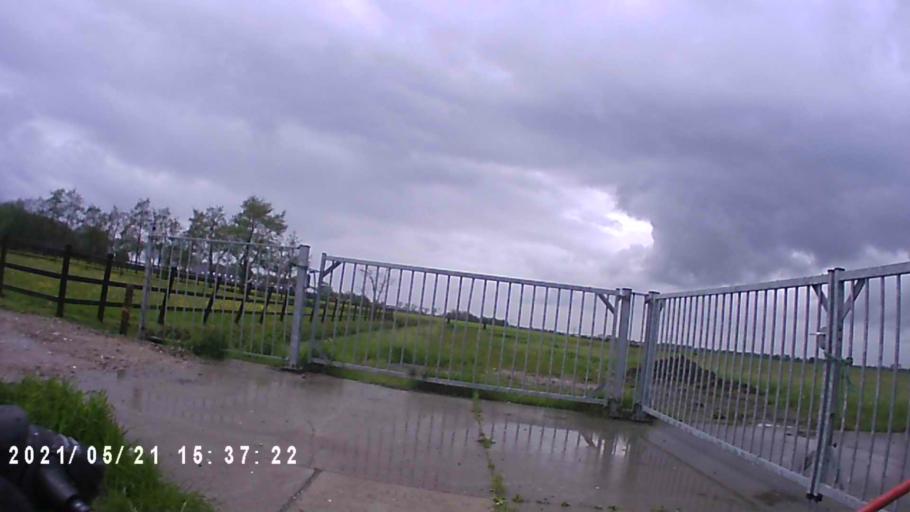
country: NL
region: Groningen
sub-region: Gemeente Zuidhorn
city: Aduard
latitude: 53.2089
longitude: 6.4641
